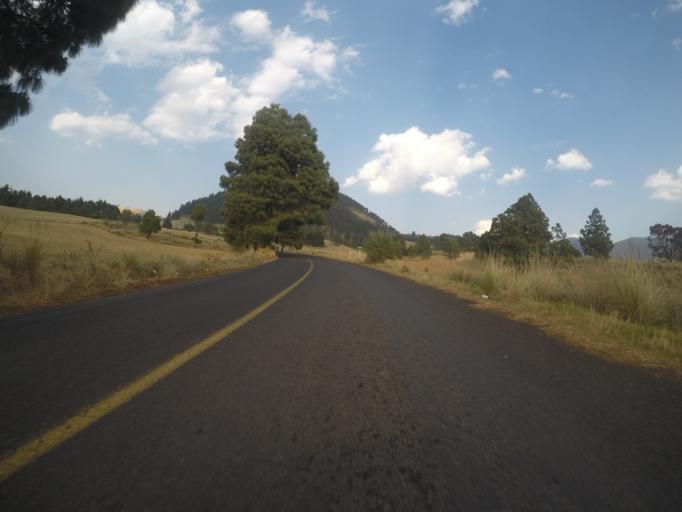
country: MX
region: Mexico
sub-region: Xalatlaco
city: San Juan Tomasquillo Herradura
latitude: 19.1622
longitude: -99.3891
